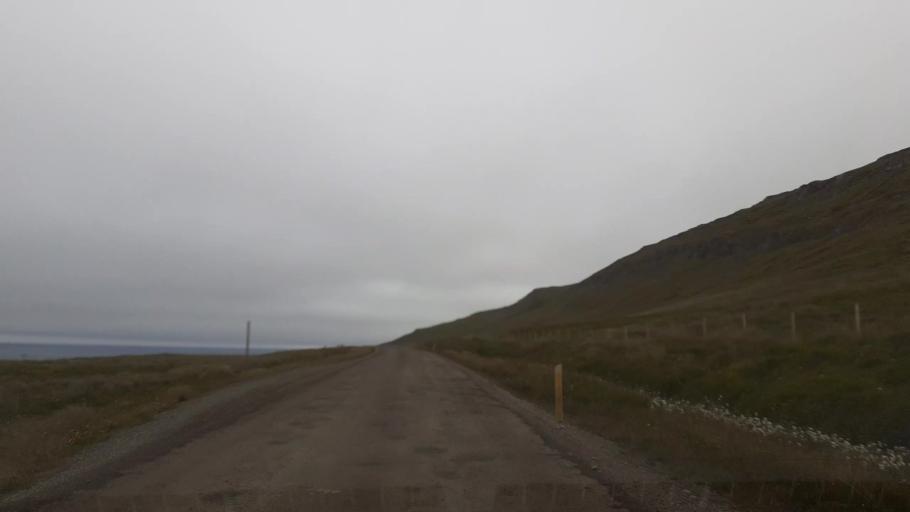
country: IS
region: Northwest
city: Saudarkrokur
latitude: 65.5083
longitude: -20.9719
